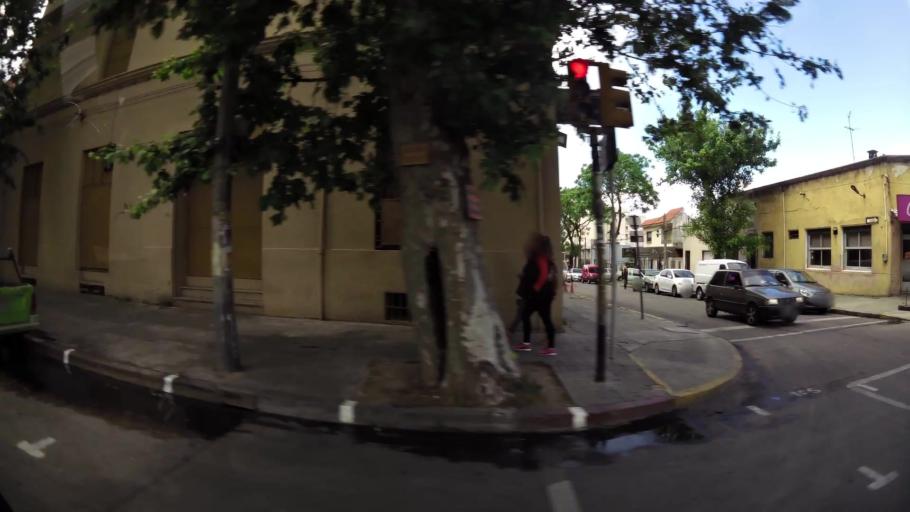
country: UY
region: Montevideo
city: Montevideo
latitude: -34.8781
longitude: -56.1458
